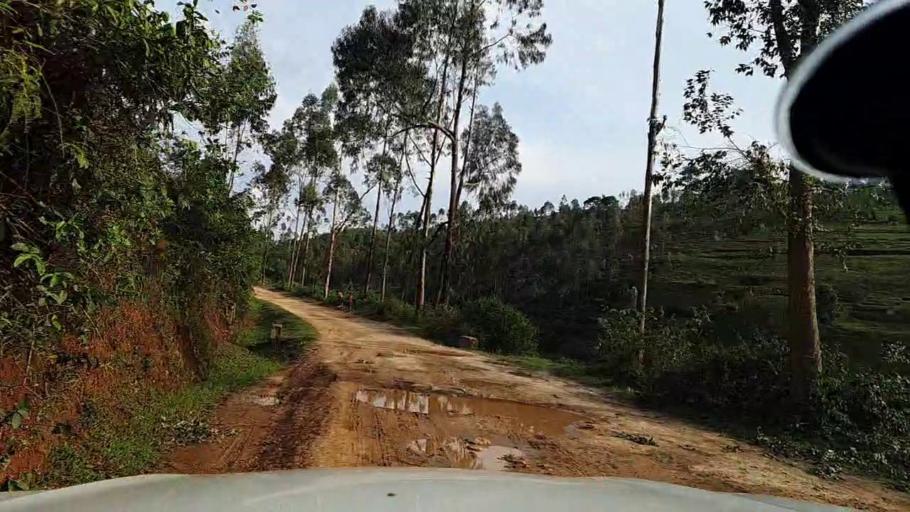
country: RW
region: Southern Province
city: Gitarama
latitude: -2.1717
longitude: 29.5536
